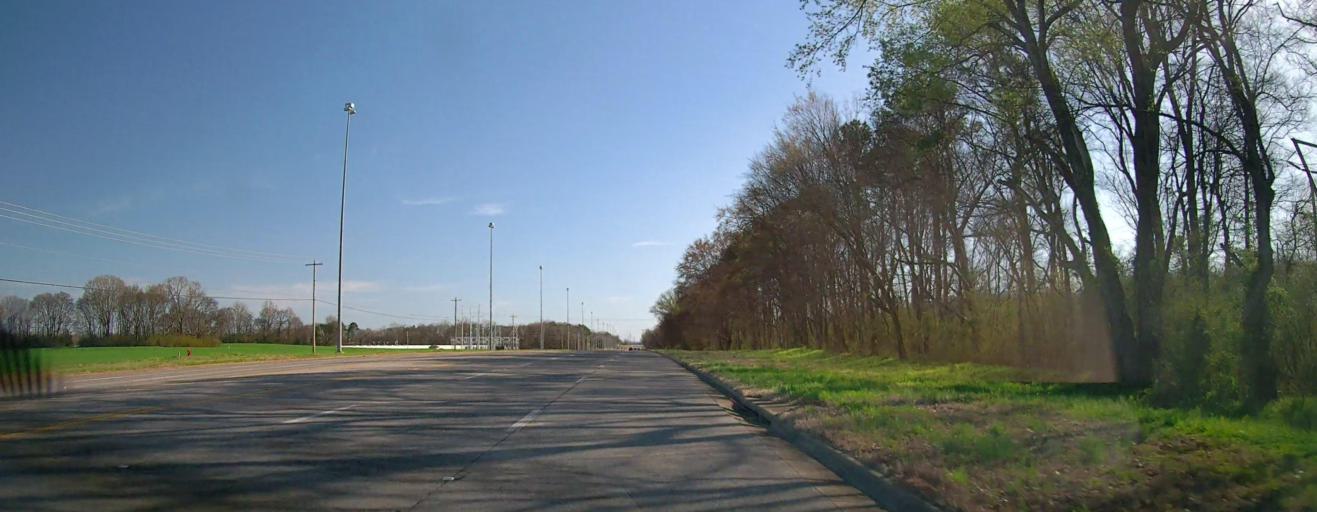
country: US
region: Alabama
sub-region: Colbert County
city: Muscle Shoals
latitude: 34.7686
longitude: -87.6348
